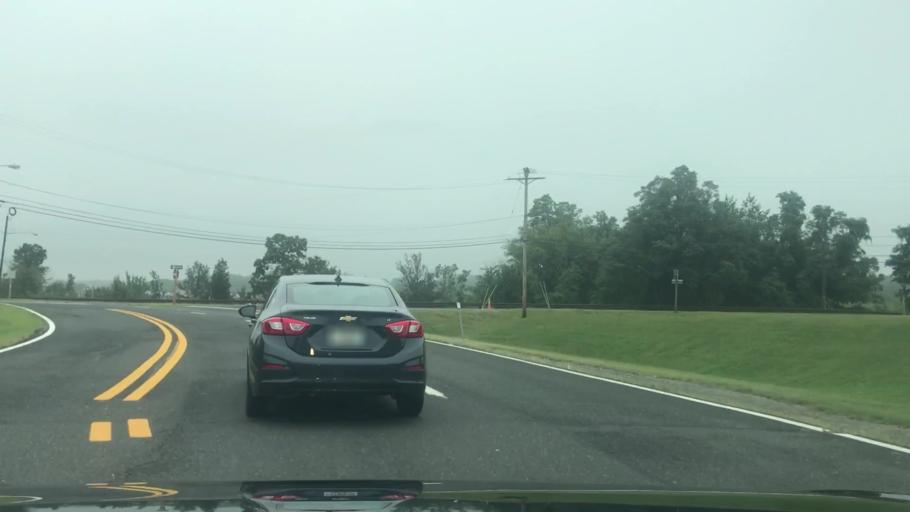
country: US
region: New Jersey
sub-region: Monmouth County
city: Strathmore
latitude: 40.3870
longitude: -74.1805
